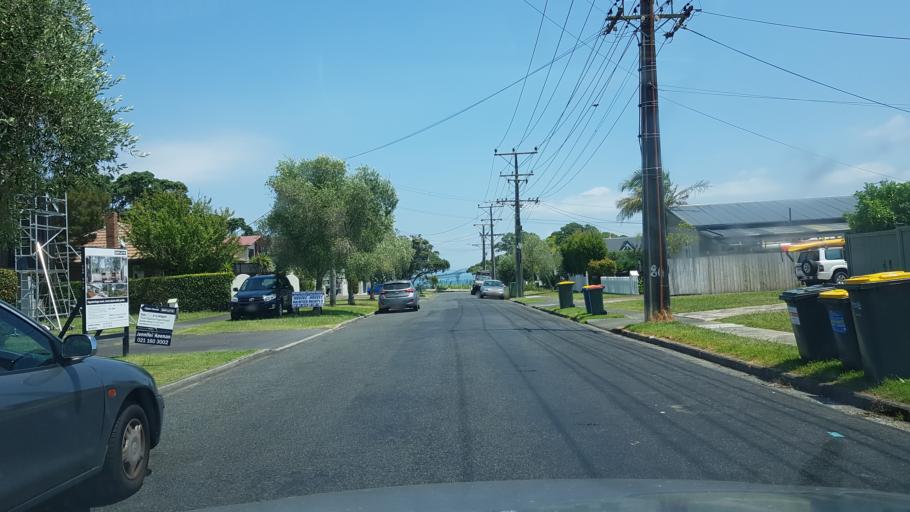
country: NZ
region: Auckland
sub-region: Auckland
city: North Shore
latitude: -36.8182
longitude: 174.7862
